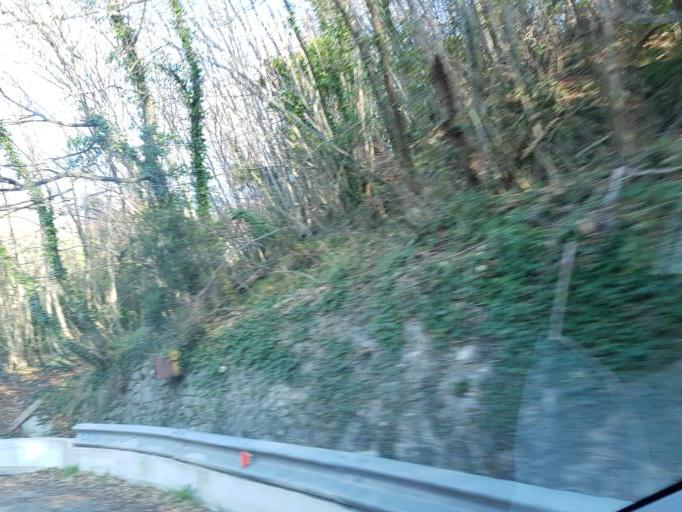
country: IT
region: Liguria
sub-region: Provincia di Genova
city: Campomorone
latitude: 44.4989
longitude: 8.8813
